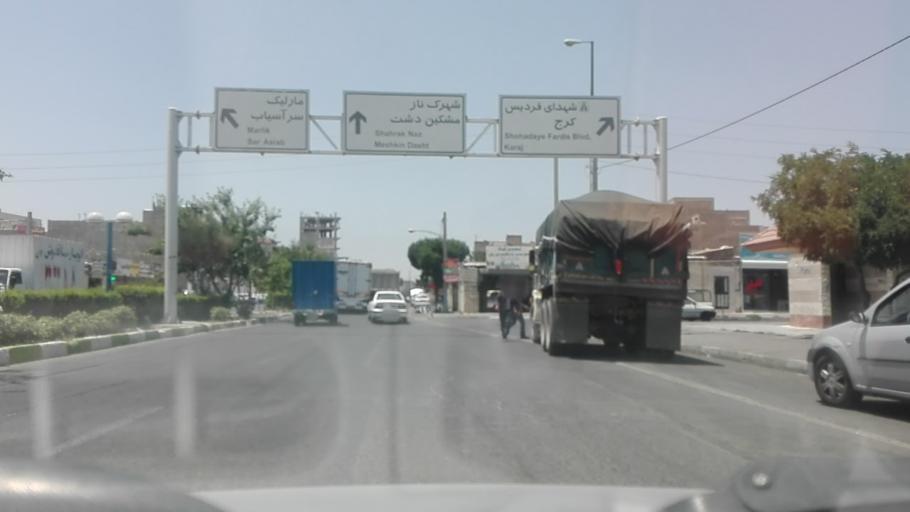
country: IR
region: Tehran
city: Shahre Jadide Andisheh
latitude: 35.7095
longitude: 50.9876
